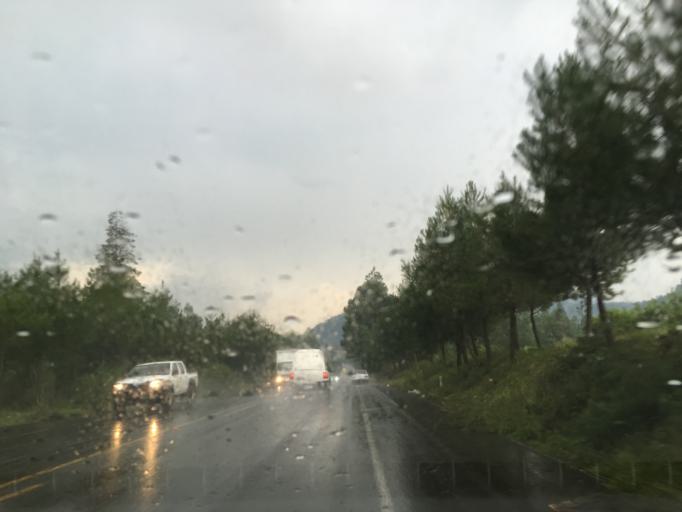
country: MX
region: Michoacan
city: Angahuan
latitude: 19.5460
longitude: -102.2089
